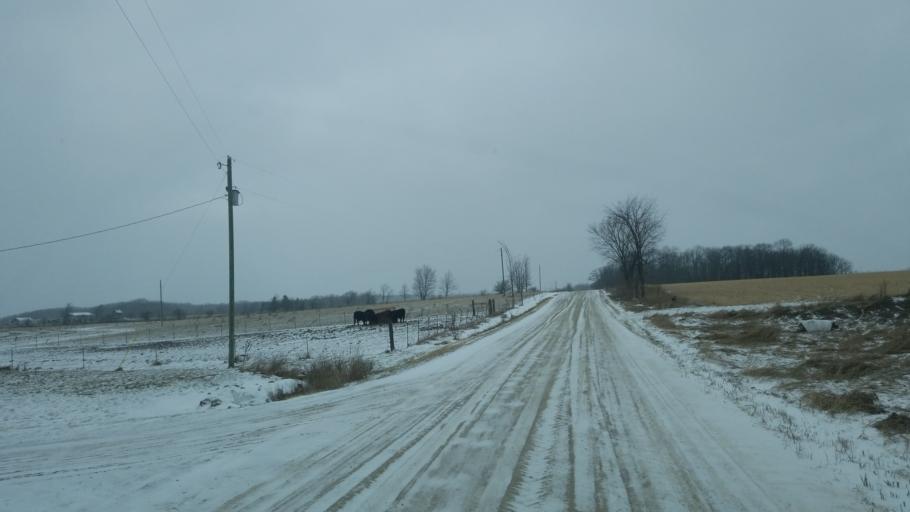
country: US
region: Michigan
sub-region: Osceola County
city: Evart
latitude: 44.0245
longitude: -85.2066
